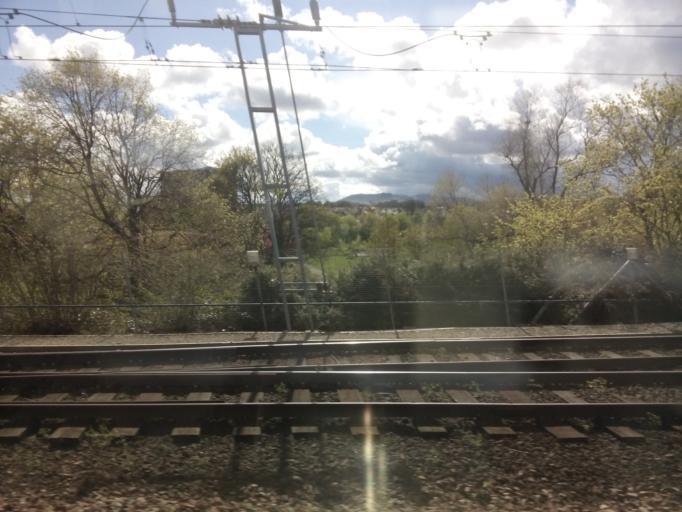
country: GB
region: Scotland
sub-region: West Lothian
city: Seafield
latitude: 55.9519
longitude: -3.1224
